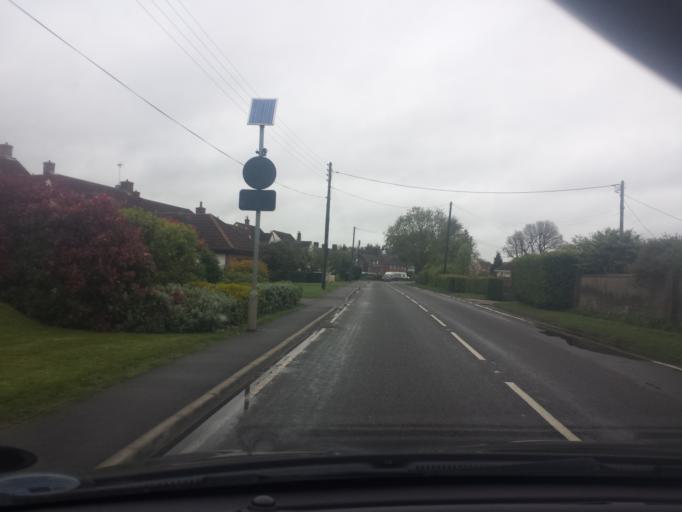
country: GB
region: England
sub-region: Essex
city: Great Bentley
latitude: 51.8715
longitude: 1.0354
